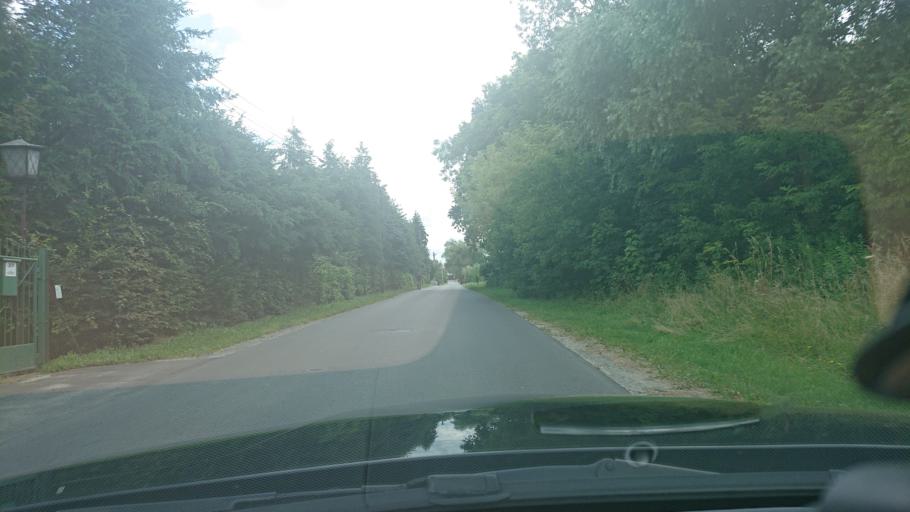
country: PL
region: Greater Poland Voivodeship
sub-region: Powiat gnieznienski
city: Gniezno
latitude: 52.5182
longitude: 17.6188
